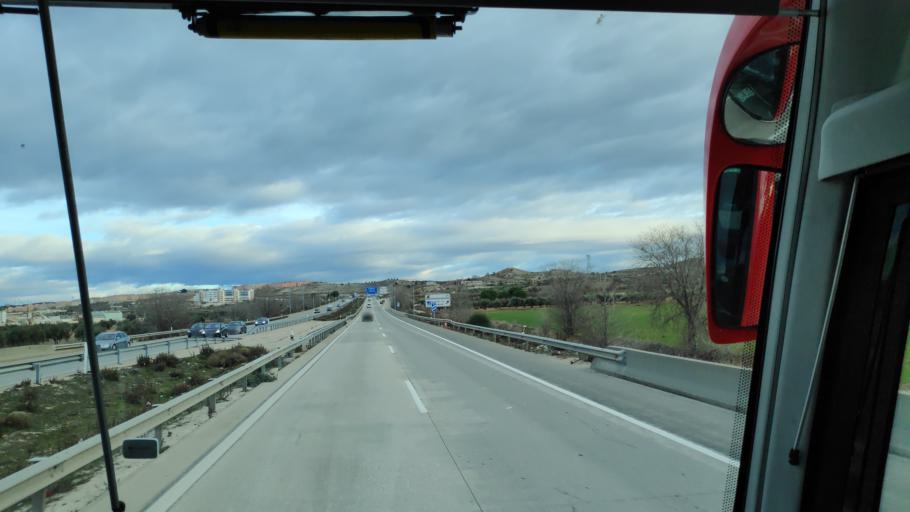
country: ES
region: Madrid
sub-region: Provincia de Madrid
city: Arganda
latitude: 40.2978
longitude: -3.4770
